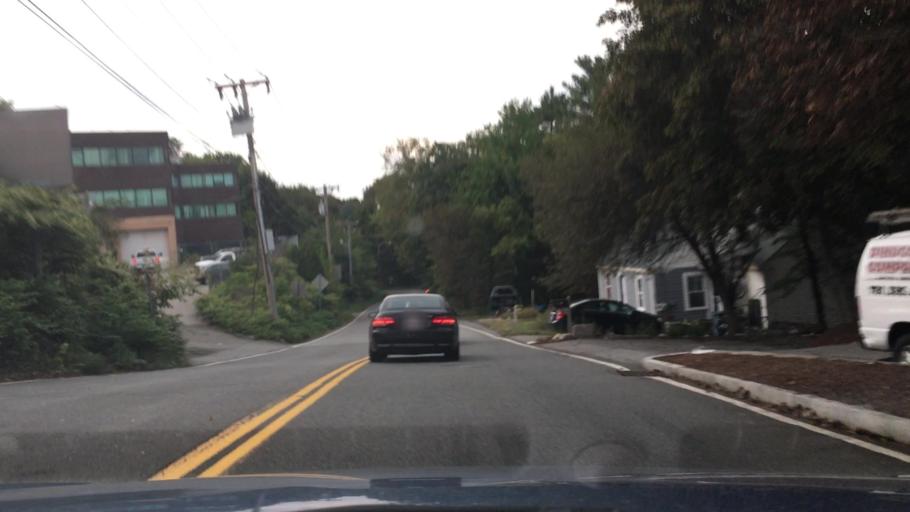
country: US
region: Massachusetts
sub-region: Middlesex County
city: Billerica
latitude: 42.5430
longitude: -71.2525
